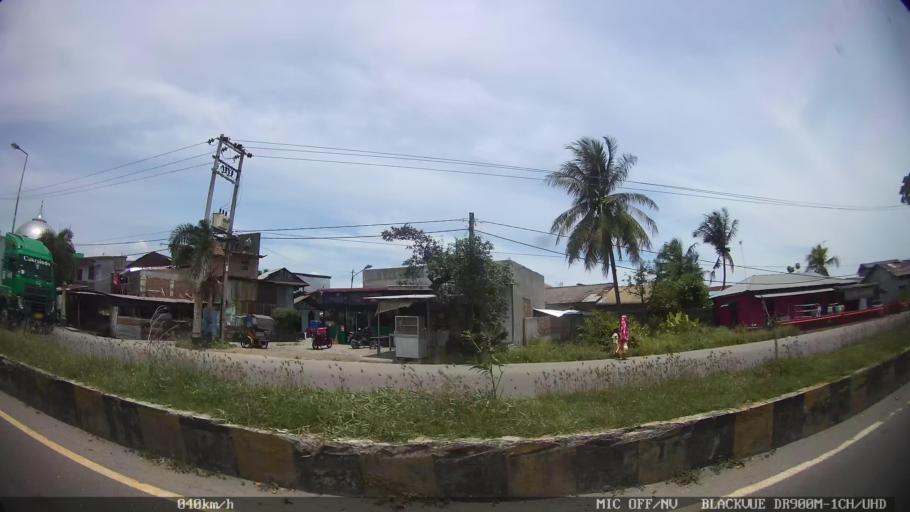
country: ID
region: North Sumatra
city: Belawan
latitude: 3.7720
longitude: 98.6828
